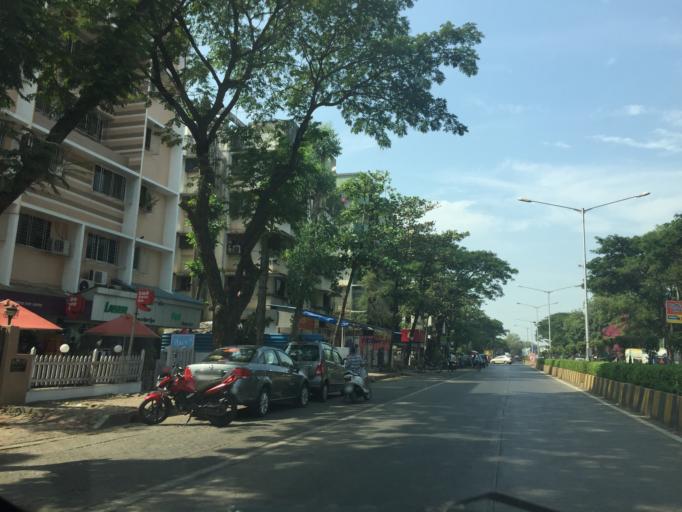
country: IN
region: Maharashtra
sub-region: Mumbai Suburban
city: Borivli
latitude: 19.2327
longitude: 72.8269
